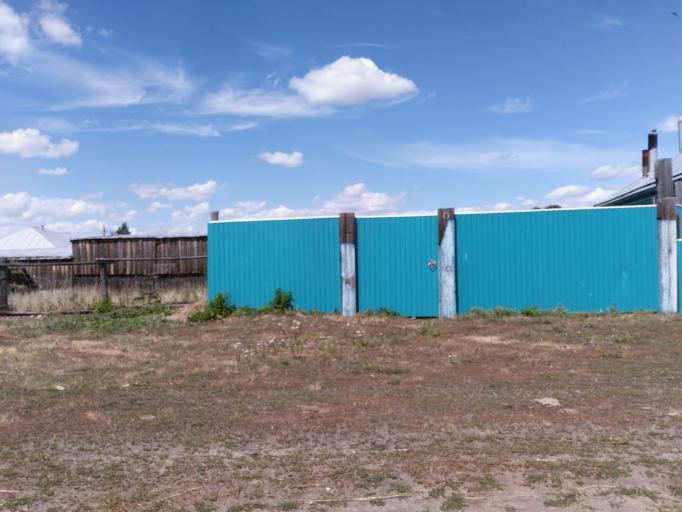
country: RU
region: Bashkortostan
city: Akhunovo
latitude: 54.1988
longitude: 59.5890
